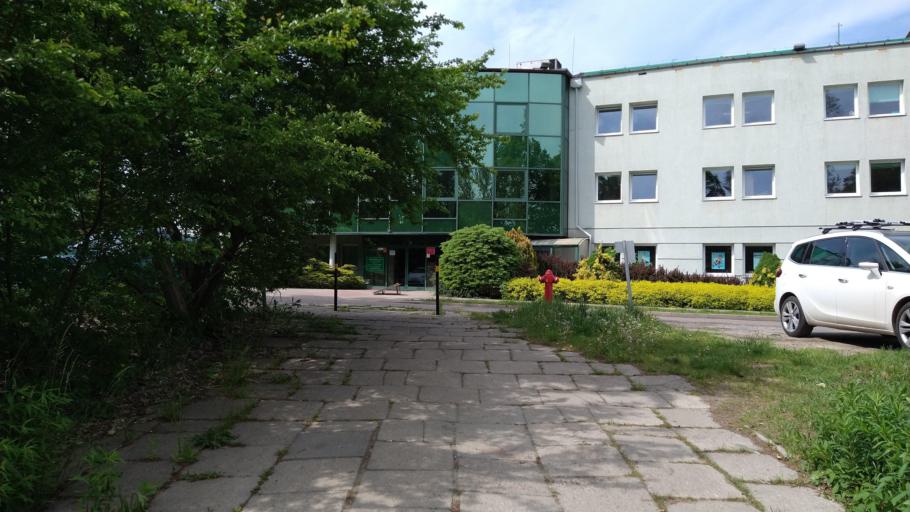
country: PL
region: Warmian-Masurian Voivodeship
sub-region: Powiat olsztynski
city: Olsztyn
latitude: 53.7957
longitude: 20.5402
